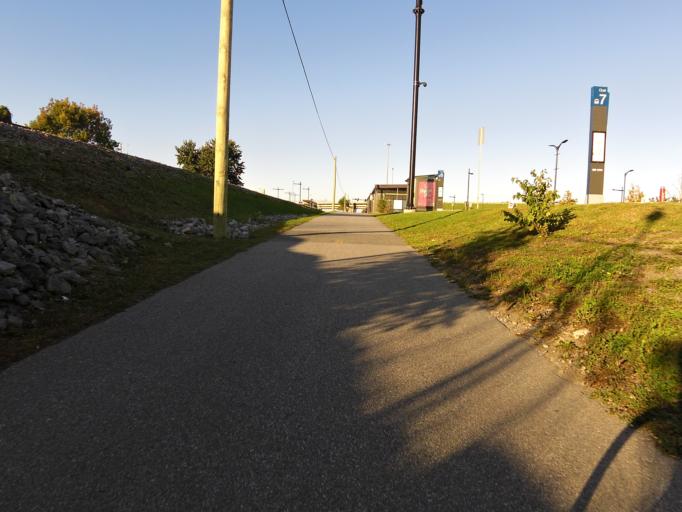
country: CA
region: Quebec
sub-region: Outaouais
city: Gatineau
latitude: 45.4682
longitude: -75.7174
